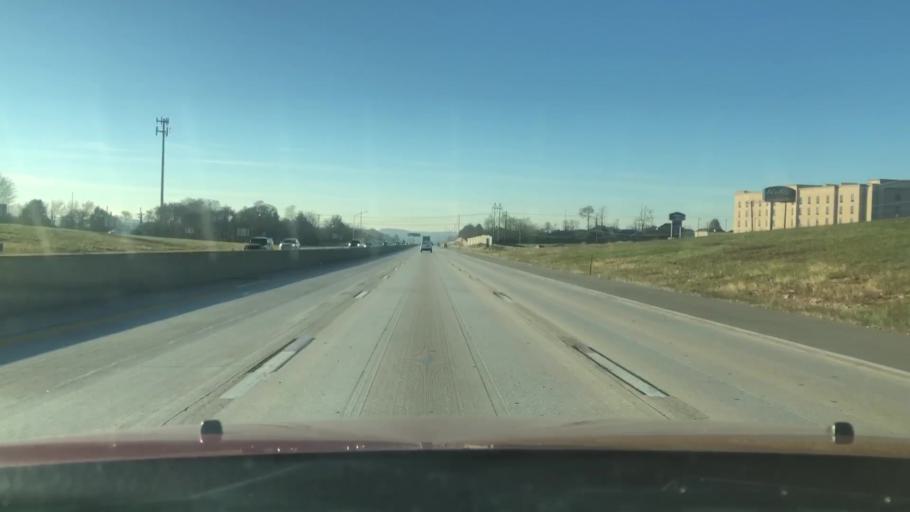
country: US
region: Missouri
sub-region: Greene County
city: Springfield
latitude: 37.1575
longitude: -93.2246
